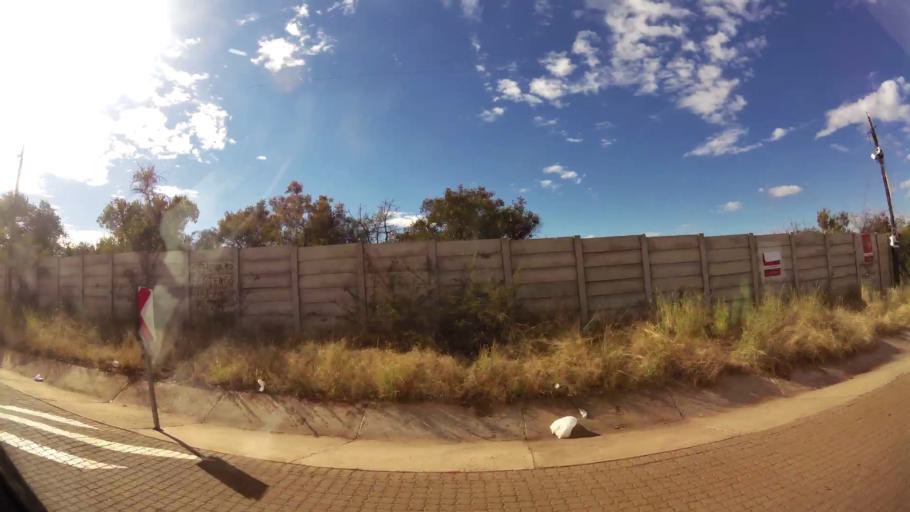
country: ZA
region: Limpopo
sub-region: Waterberg District Municipality
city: Warmbaths
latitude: -24.8765
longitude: 28.2734
